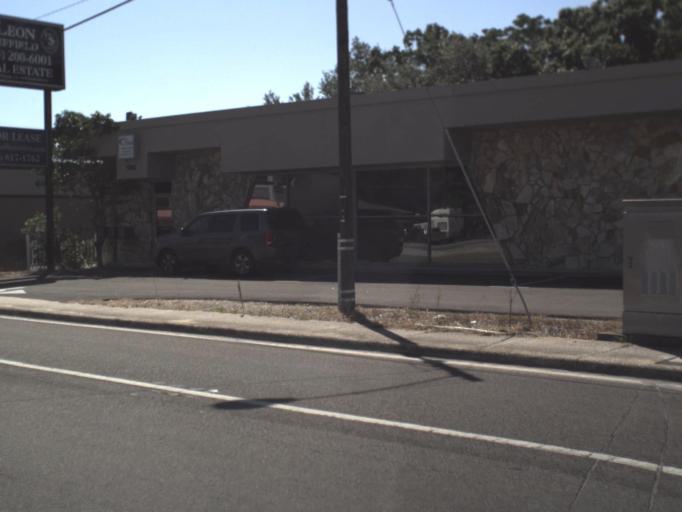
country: US
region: Florida
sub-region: Hillsborough County
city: Tampa
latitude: 27.9447
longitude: -82.4950
